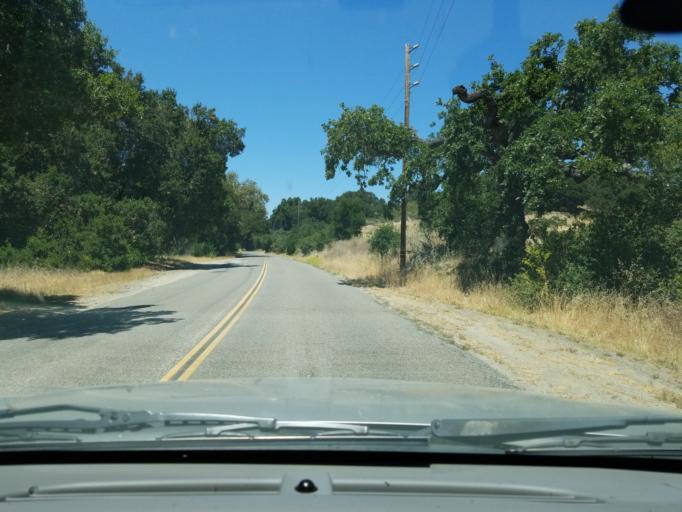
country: US
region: California
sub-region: Monterey County
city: Carmel Valley Village
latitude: 36.4310
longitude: -121.6238
